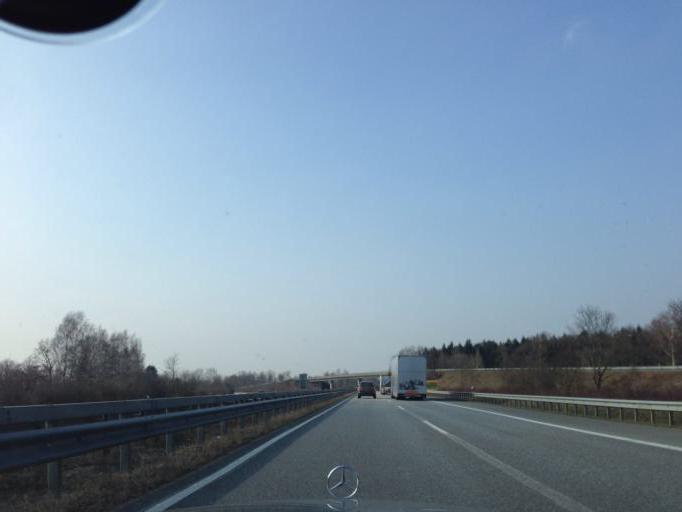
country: DE
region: Schleswig-Holstein
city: Negernbotel
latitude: 53.9678
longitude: 10.2487
